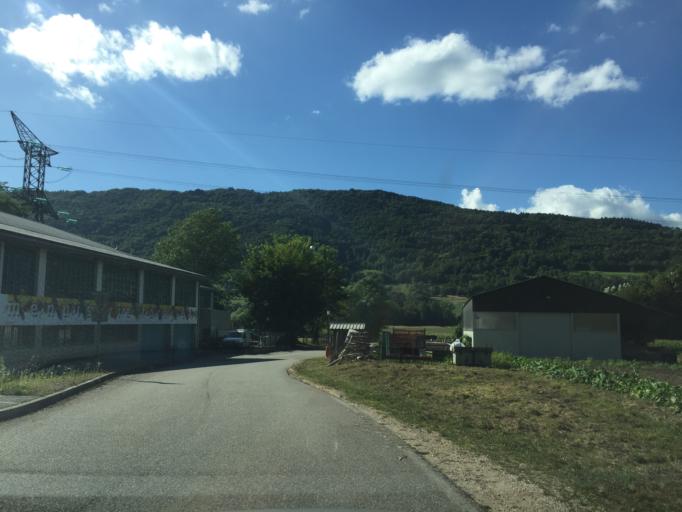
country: FR
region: Rhone-Alpes
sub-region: Departement de la Savoie
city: Coise-Saint-Jean-Pied-Gauthier
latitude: 45.4951
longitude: 6.1613
